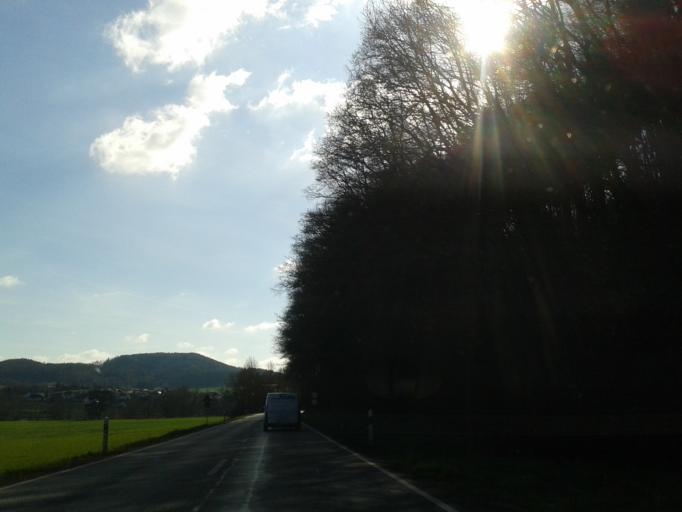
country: DE
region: Hesse
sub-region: Regierungsbezirk Giessen
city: Biedenkopf
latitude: 50.8614
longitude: 8.5753
